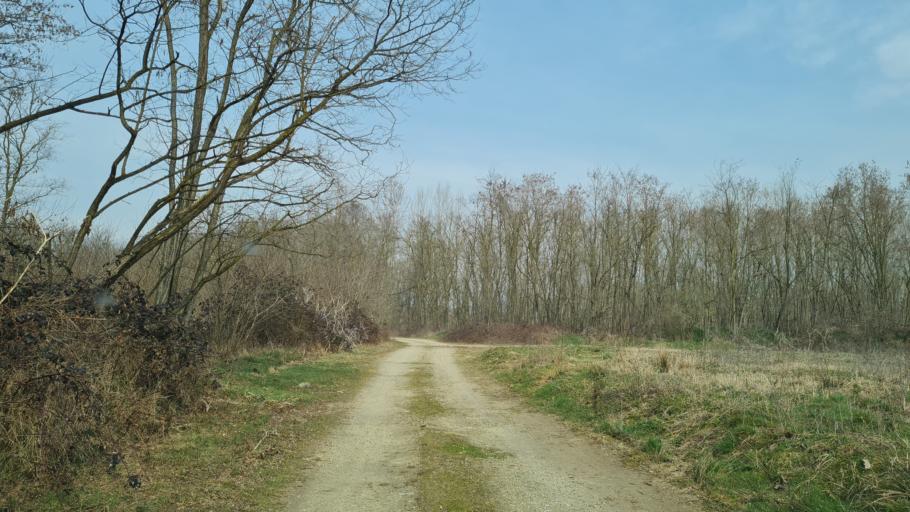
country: IT
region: Piedmont
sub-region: Provincia di Biella
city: Salussola
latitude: 45.4547
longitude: 8.1023
